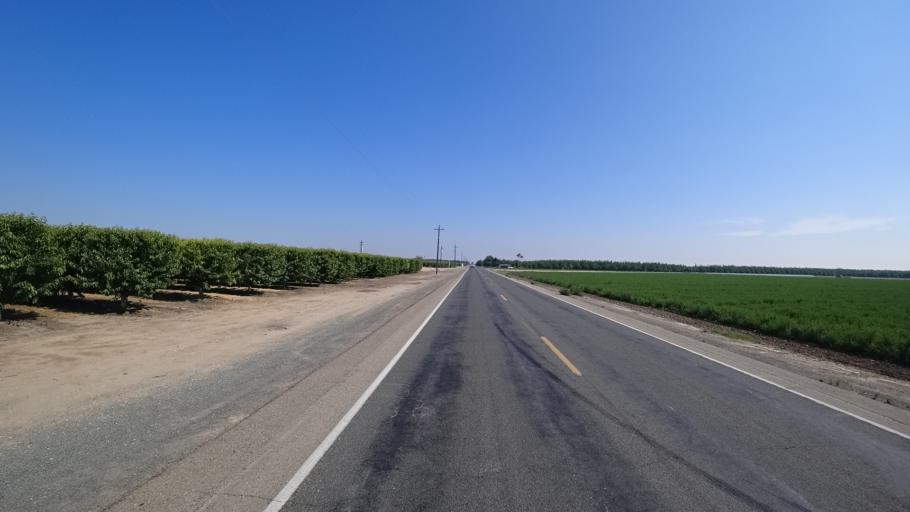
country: US
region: California
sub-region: Fresno County
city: Kingsburg
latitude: 36.4197
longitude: -119.5648
